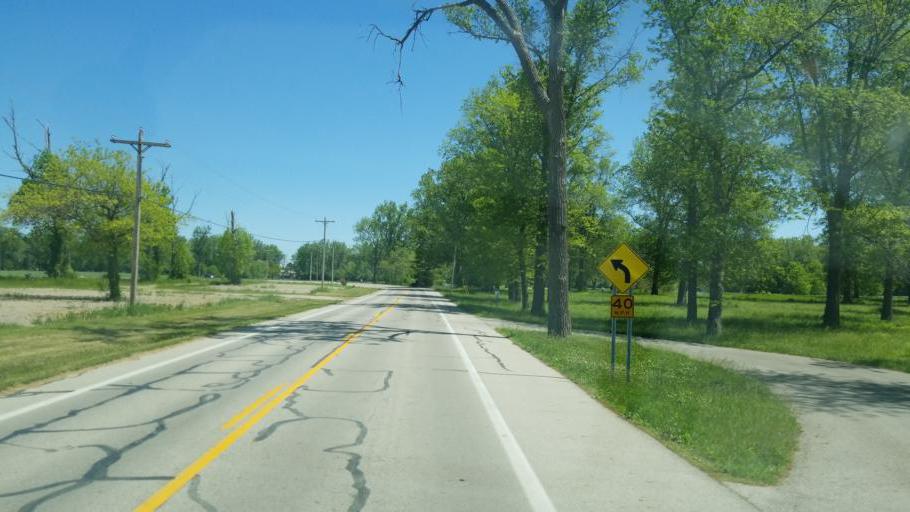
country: US
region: Ohio
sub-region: Auglaize County
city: Minster
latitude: 40.3751
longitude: -84.3599
